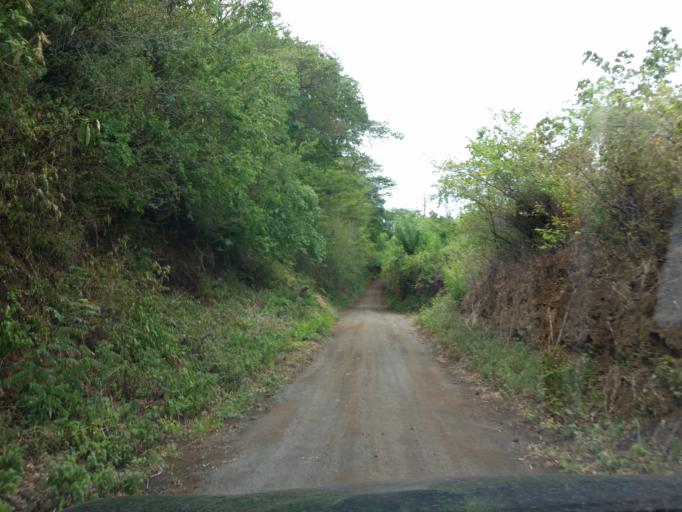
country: NI
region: Managua
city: El Crucero
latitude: 11.9926
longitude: -86.3671
